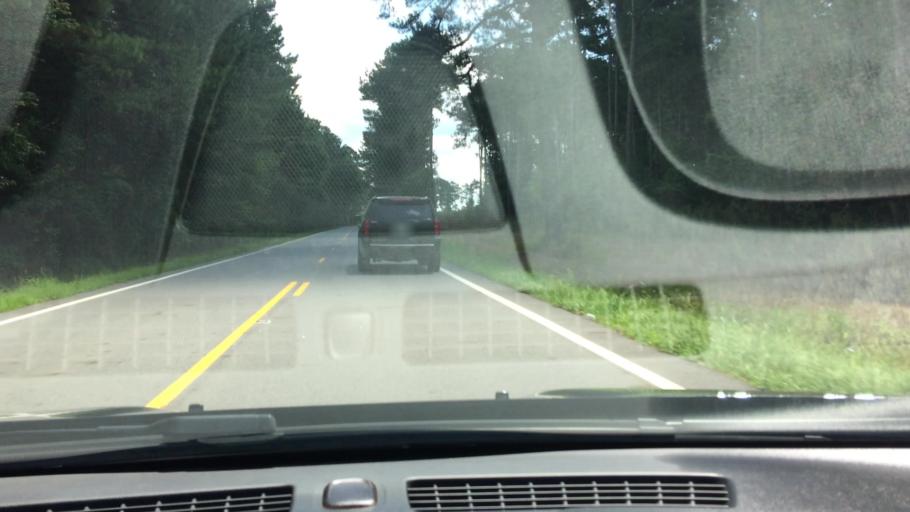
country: US
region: North Carolina
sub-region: Craven County
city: Vanceboro
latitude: 35.4284
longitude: -77.2077
